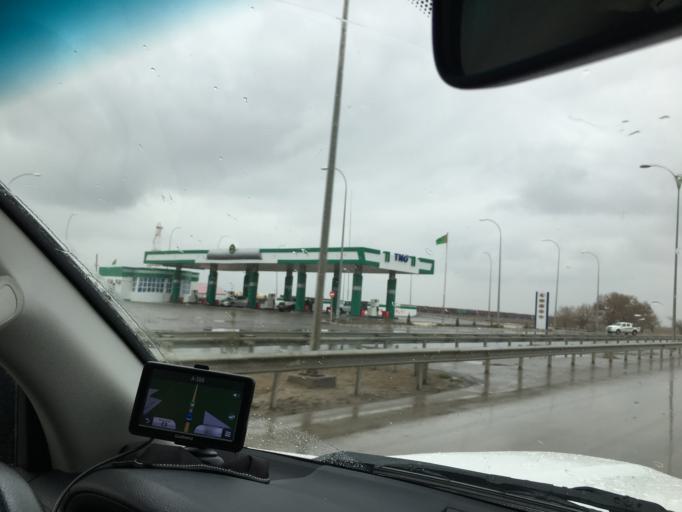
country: TM
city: Murgab
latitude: 37.5001
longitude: 61.9598
